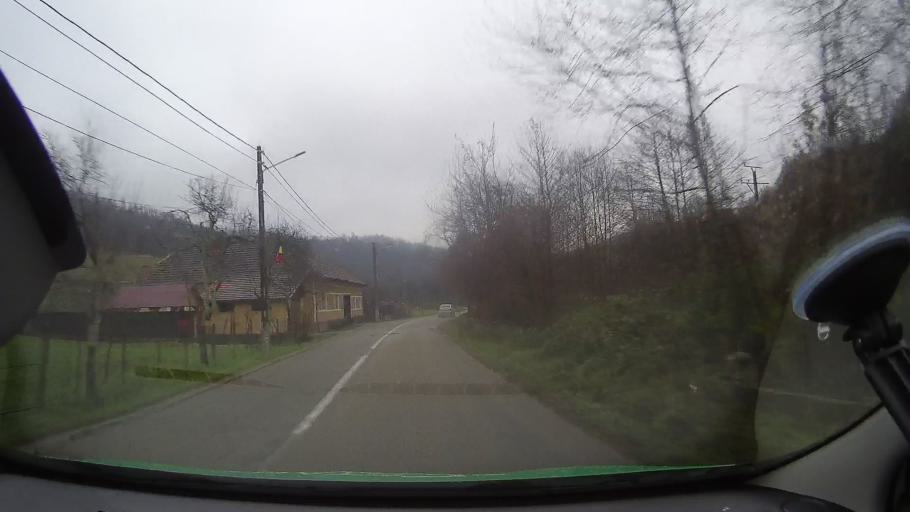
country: RO
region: Arad
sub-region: Comuna Moneasa
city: Moneasa
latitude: 46.4343
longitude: 22.2509
